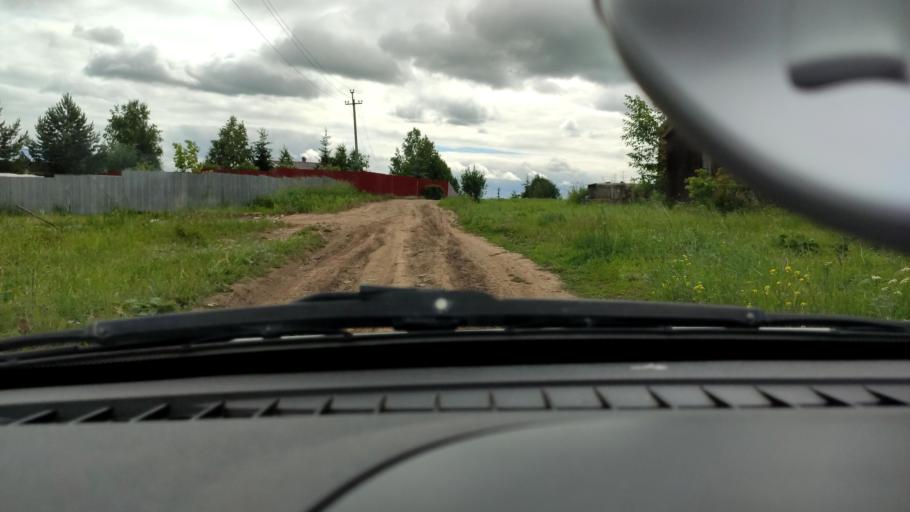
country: RU
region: Perm
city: Ferma
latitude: 57.9122
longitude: 56.3172
